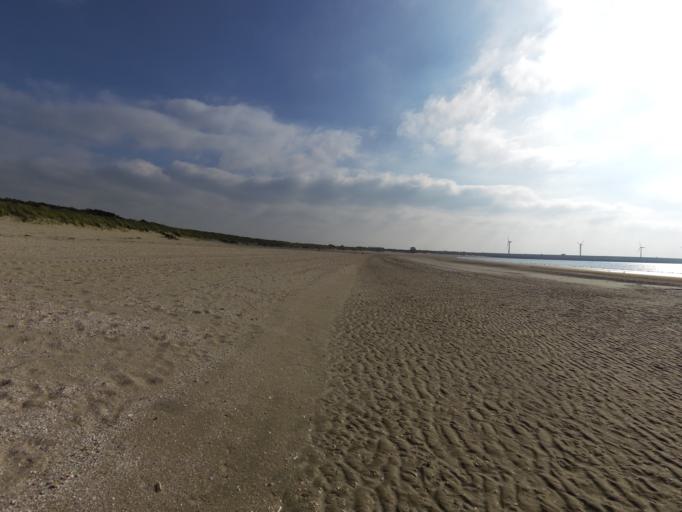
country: NL
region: South Holland
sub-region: Gemeente Hellevoetsluis
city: Nieuw-Helvoet
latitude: 51.8527
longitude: 4.0656
